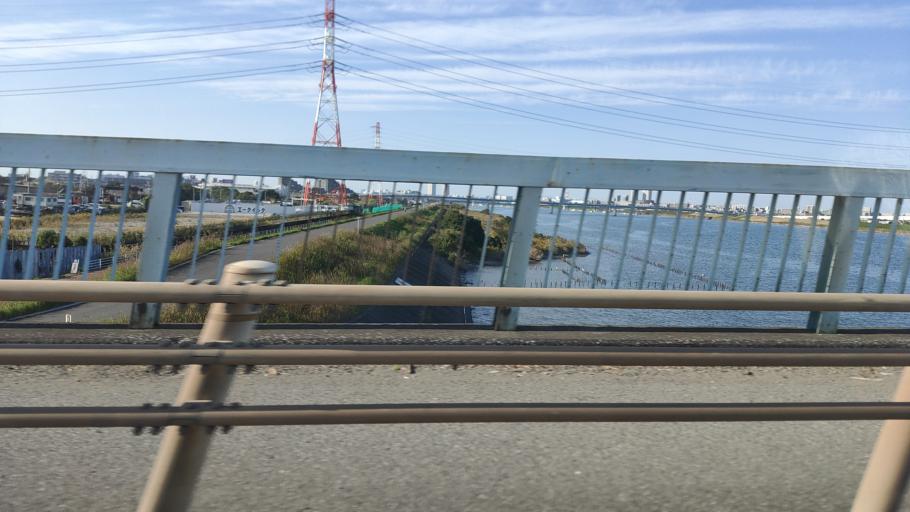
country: JP
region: Chiba
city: Funabashi
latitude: 35.6831
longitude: 139.9387
